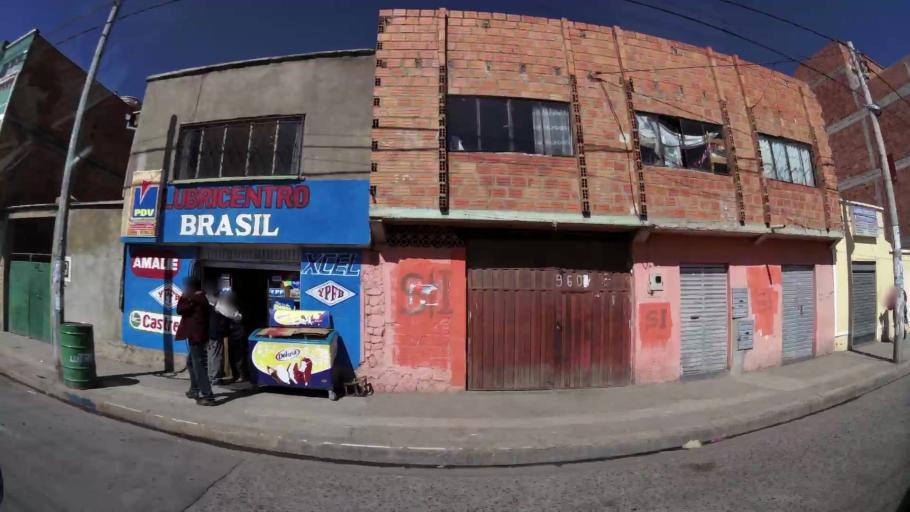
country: BO
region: La Paz
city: La Paz
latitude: -16.5224
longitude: -68.1551
